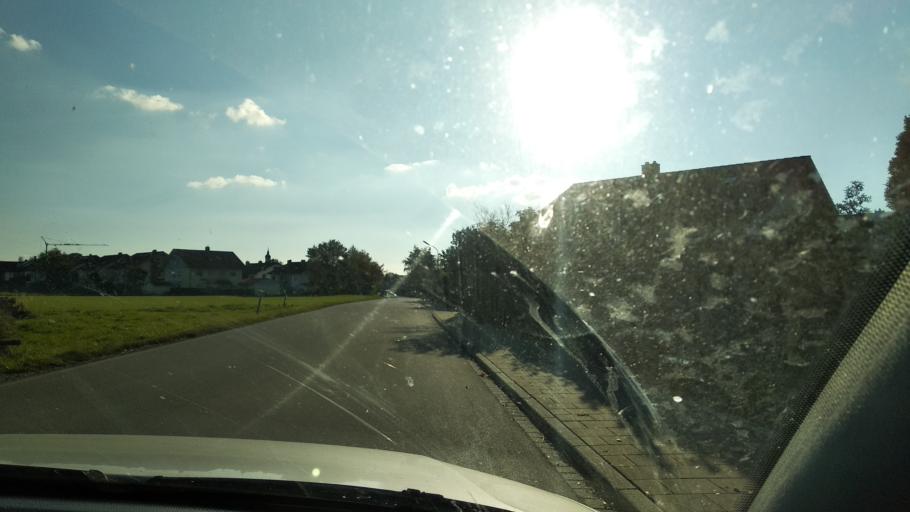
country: DE
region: Bavaria
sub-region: Upper Bavaria
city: Hohenkirchen-Siegertsbrunn
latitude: 48.0264
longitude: 11.7329
